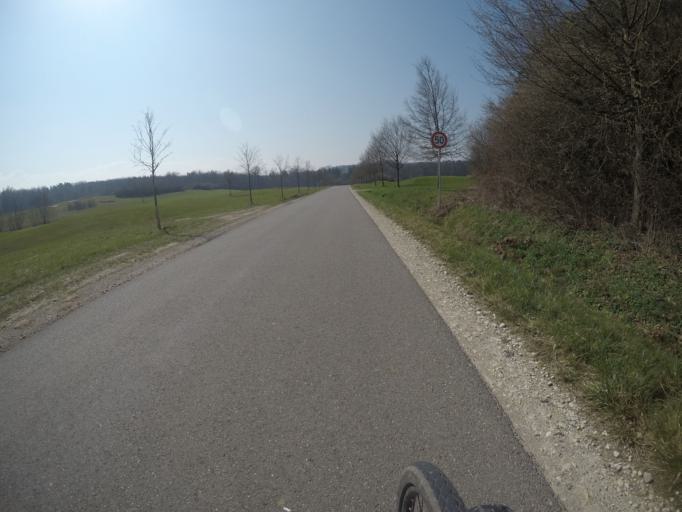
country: DE
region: Baden-Wuerttemberg
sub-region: Tuebingen Region
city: Pliezhausen
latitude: 48.5742
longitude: 9.2171
